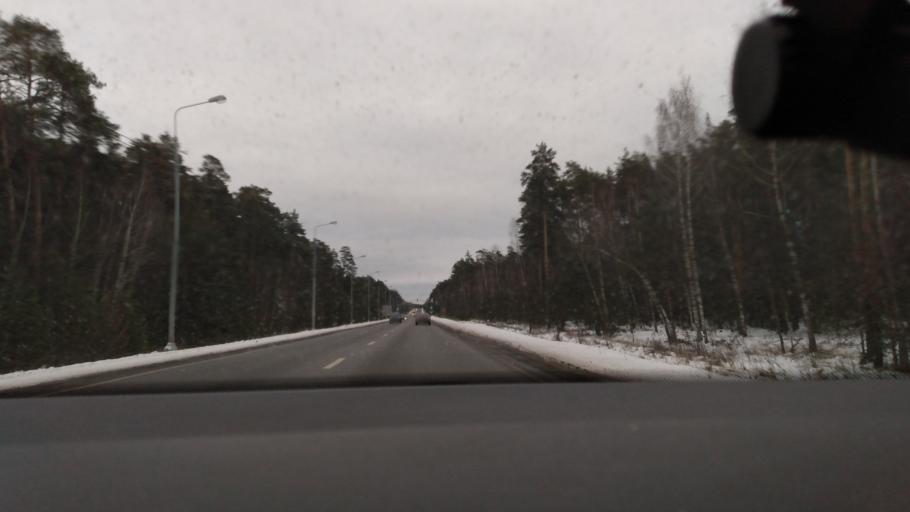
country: RU
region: Moskovskaya
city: Il'inskiy Pogost
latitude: 55.4884
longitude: 38.8872
